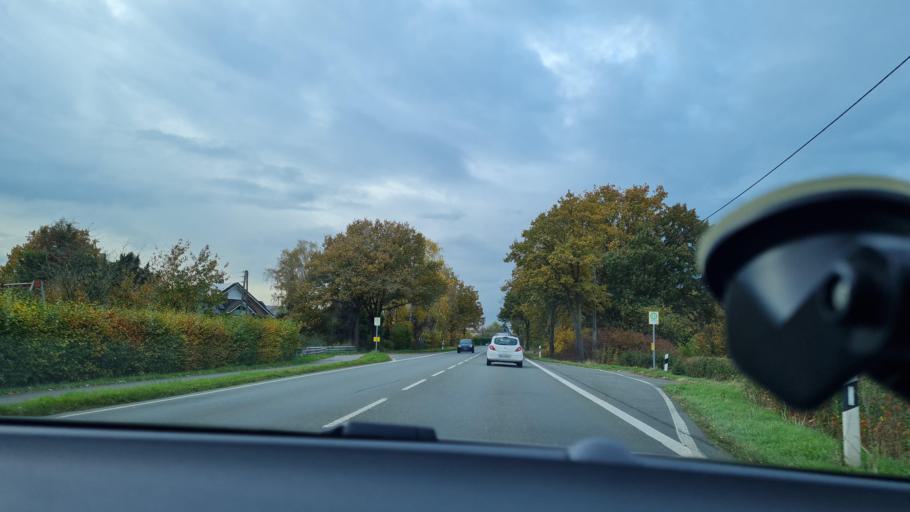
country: DE
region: North Rhine-Westphalia
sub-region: Regierungsbezirk Dusseldorf
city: Voerde
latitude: 51.6174
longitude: 6.6843
